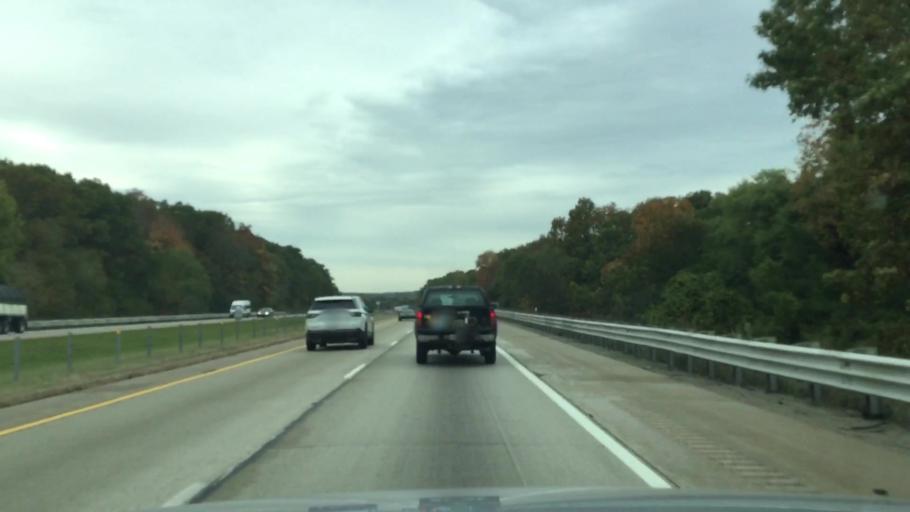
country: US
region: Michigan
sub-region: Calhoun County
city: Brownlee Park
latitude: 42.2857
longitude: -85.1416
